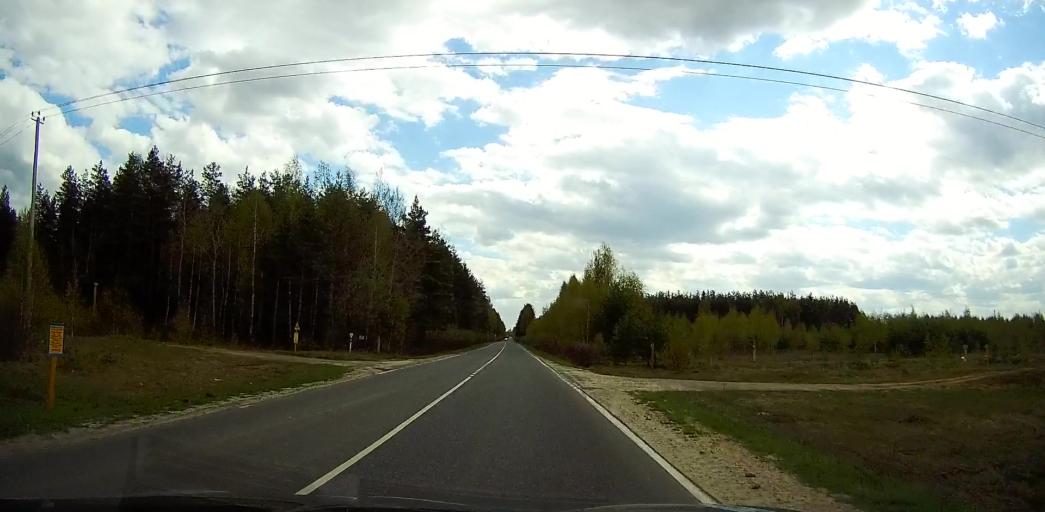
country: RU
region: Moskovskaya
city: Davydovo
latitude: 55.6590
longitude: 38.7540
